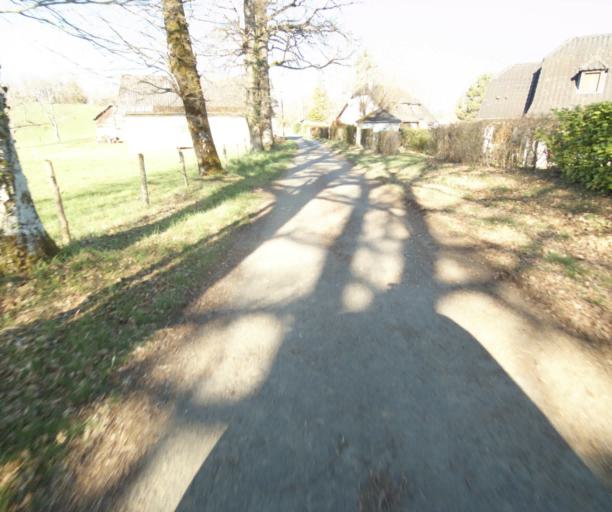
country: FR
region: Limousin
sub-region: Departement de la Correze
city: Seilhac
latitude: 45.3731
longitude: 1.7495
